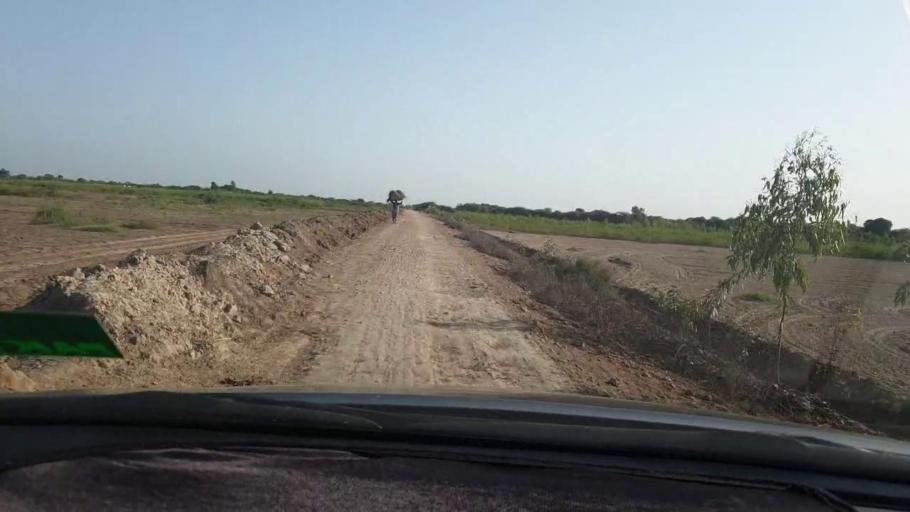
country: PK
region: Sindh
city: Naukot
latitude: 24.9090
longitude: 69.2765
